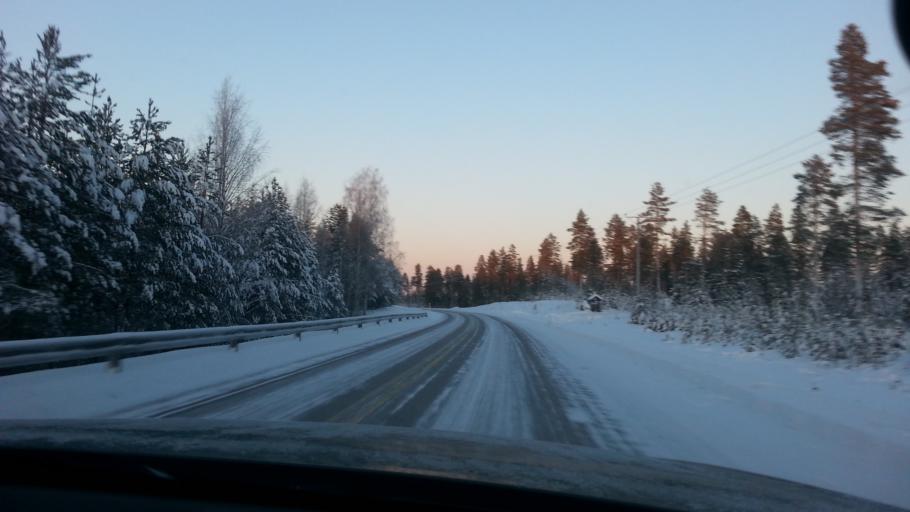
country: FI
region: Lapland
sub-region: Rovaniemi
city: Rovaniemi
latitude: 66.7855
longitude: 25.4436
